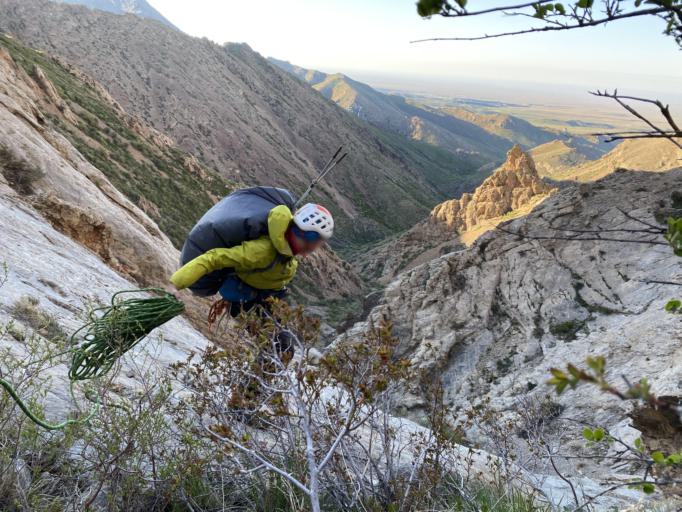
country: KZ
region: Ongtustik Qazaqstan
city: Ashchysay
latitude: 43.7655
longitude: 68.7779
